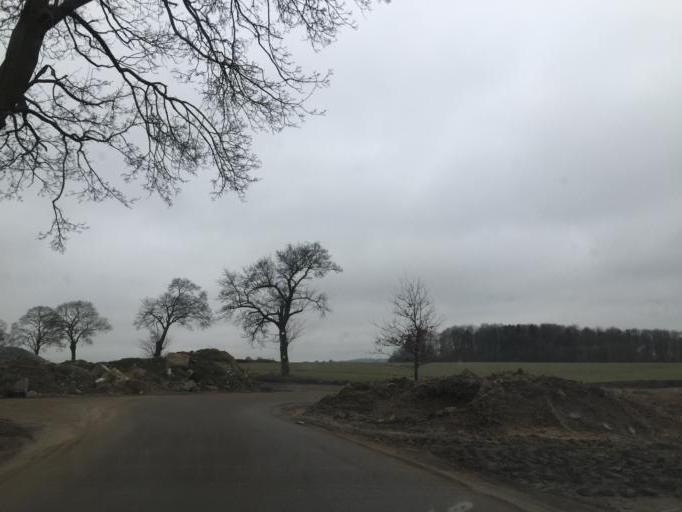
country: PL
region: Pomeranian Voivodeship
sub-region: Powiat kartuski
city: Banino
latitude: 54.4051
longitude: 18.4404
